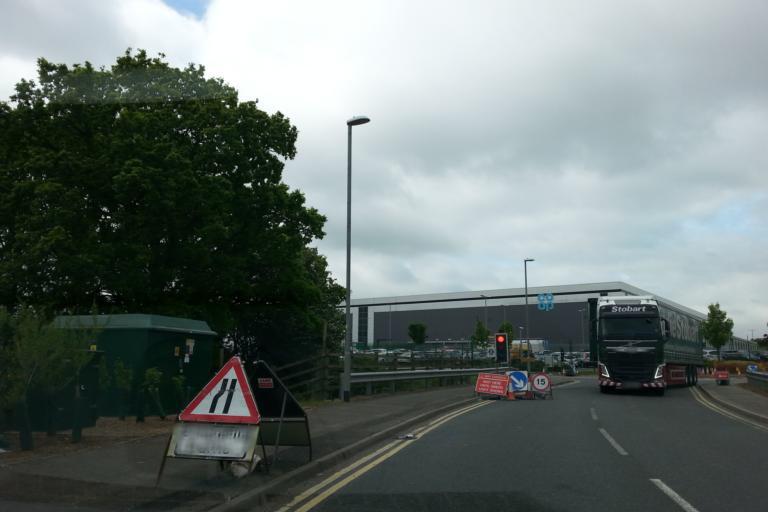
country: GB
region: England
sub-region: Derbyshire
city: Pinxton
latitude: 53.1045
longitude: -1.3156
